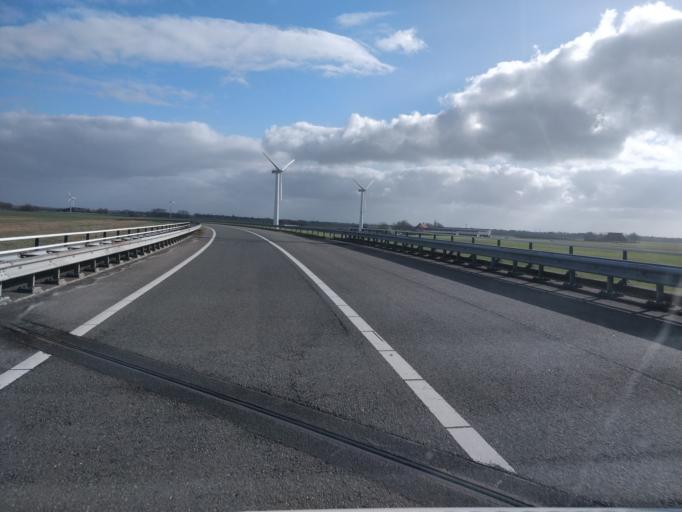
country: NL
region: Friesland
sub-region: Sudwest Fryslan
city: Makkum
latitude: 53.0970
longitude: 5.3921
